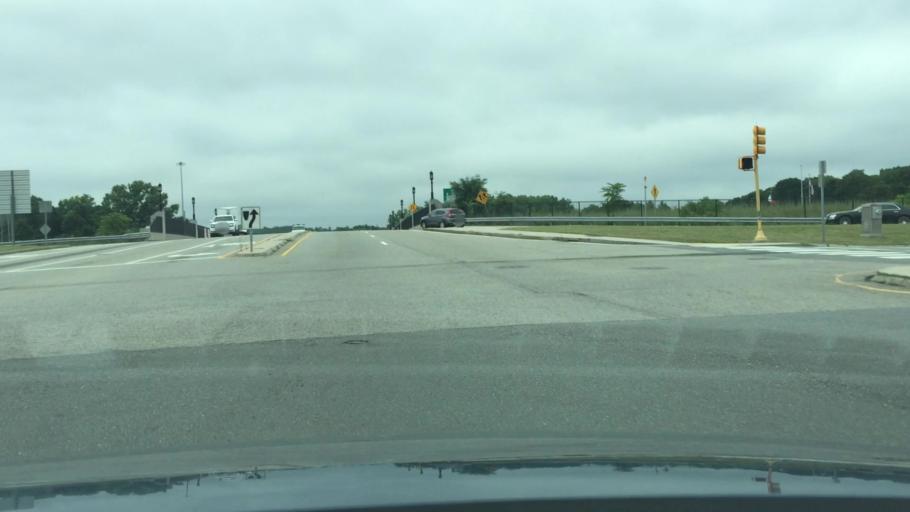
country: US
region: Massachusetts
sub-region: Middlesex County
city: Waltham
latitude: 42.3970
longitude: -71.2595
